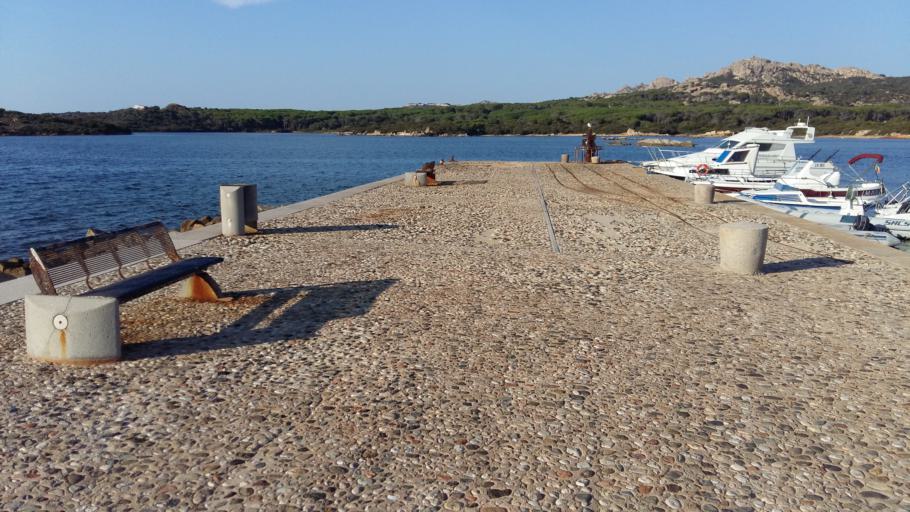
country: IT
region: Sardinia
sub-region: Provincia di Olbia-Tempio
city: La Maddalena
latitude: 41.1997
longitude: 9.4527
